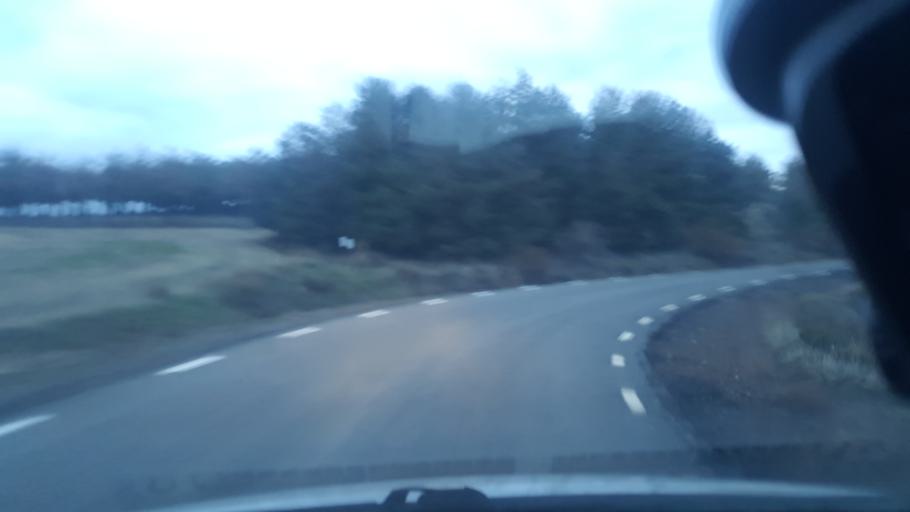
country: ES
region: Castille and Leon
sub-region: Provincia de Avila
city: Ojos-Albos
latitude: 40.7318
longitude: -4.4737
